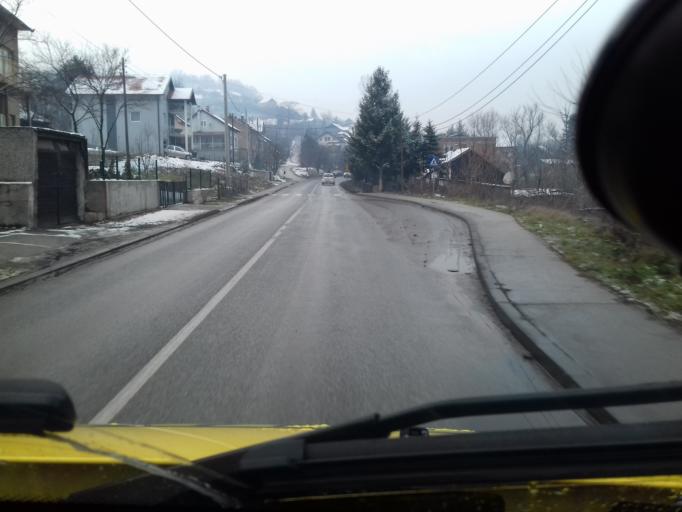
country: BA
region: Federation of Bosnia and Herzegovina
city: Zenica
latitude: 44.2125
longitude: 17.8921
